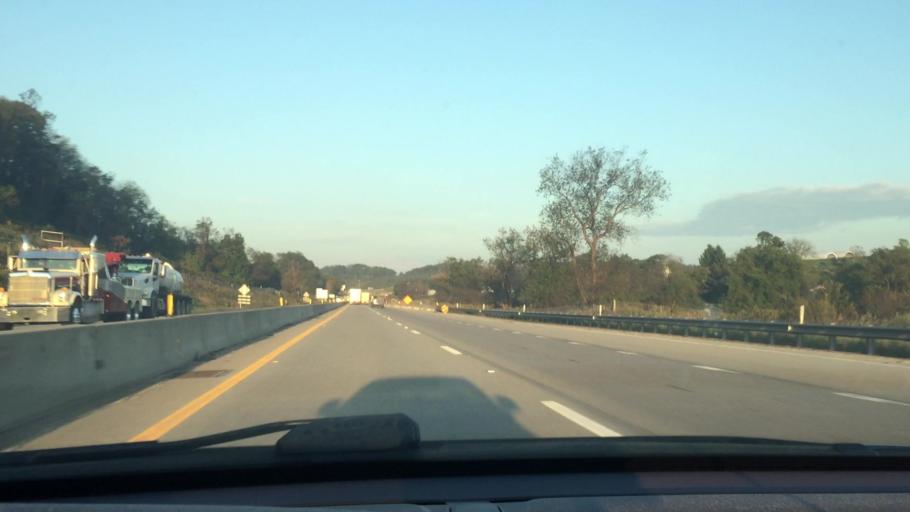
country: US
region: Pennsylvania
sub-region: Washington County
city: East Washington
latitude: 40.1572
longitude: -80.1384
